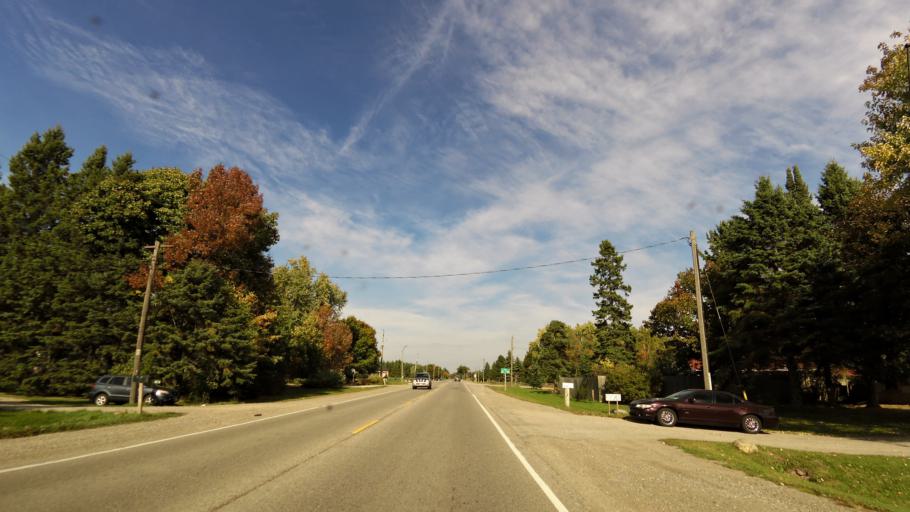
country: CA
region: Ontario
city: Orangeville
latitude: 43.7530
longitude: -80.0670
